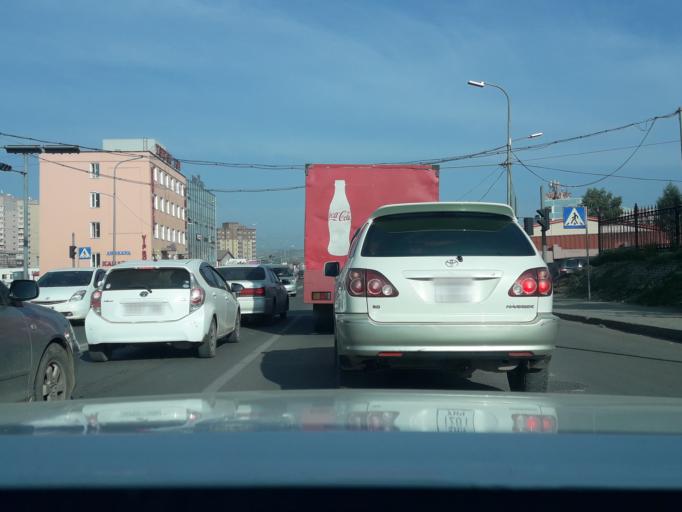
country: MN
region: Ulaanbaatar
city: Ulaanbaatar
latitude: 47.9260
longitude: 106.9444
